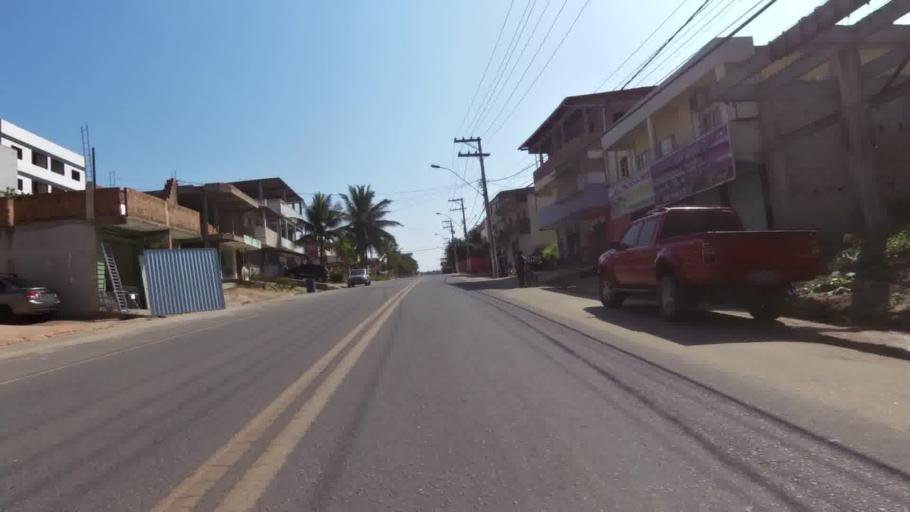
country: BR
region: Espirito Santo
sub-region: Marataizes
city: Marataizes
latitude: -21.0460
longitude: -40.8335
